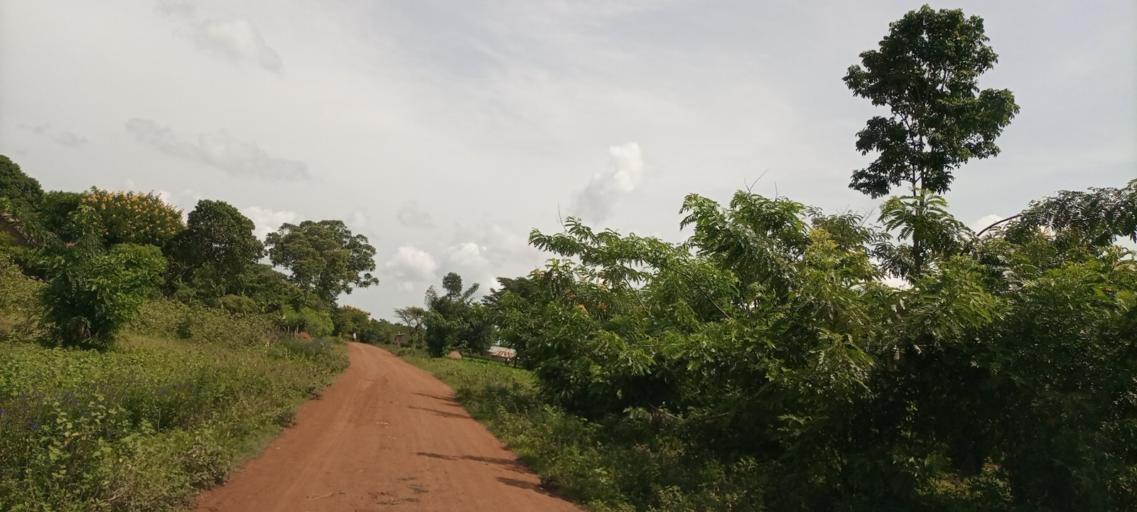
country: UG
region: Eastern Region
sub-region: Budaka District
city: Budaka
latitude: 1.1749
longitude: 33.9260
